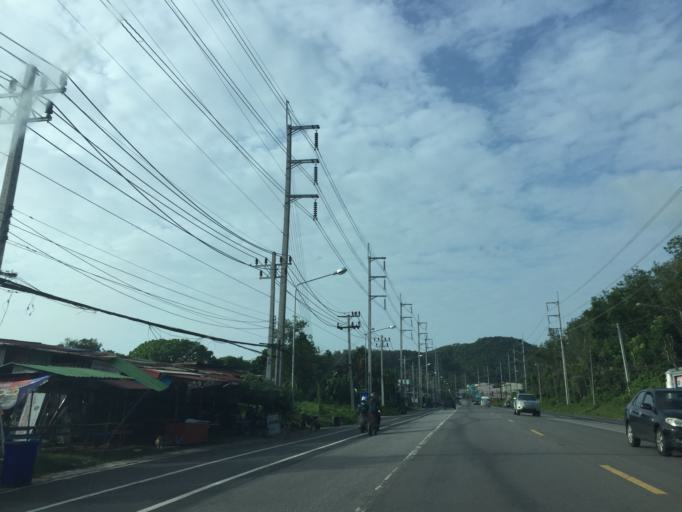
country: TH
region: Phuket
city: Mueang Phuket
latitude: 7.8506
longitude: 98.3816
